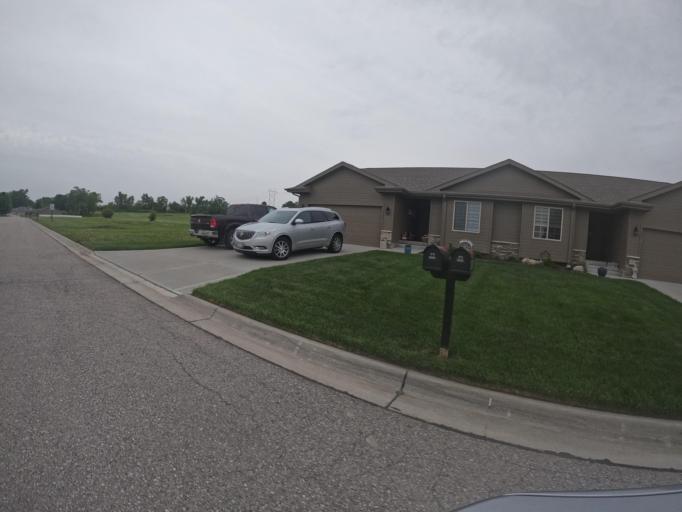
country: US
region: Nebraska
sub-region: Sarpy County
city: Offutt Air Force Base
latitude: 41.0493
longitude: -95.9580
